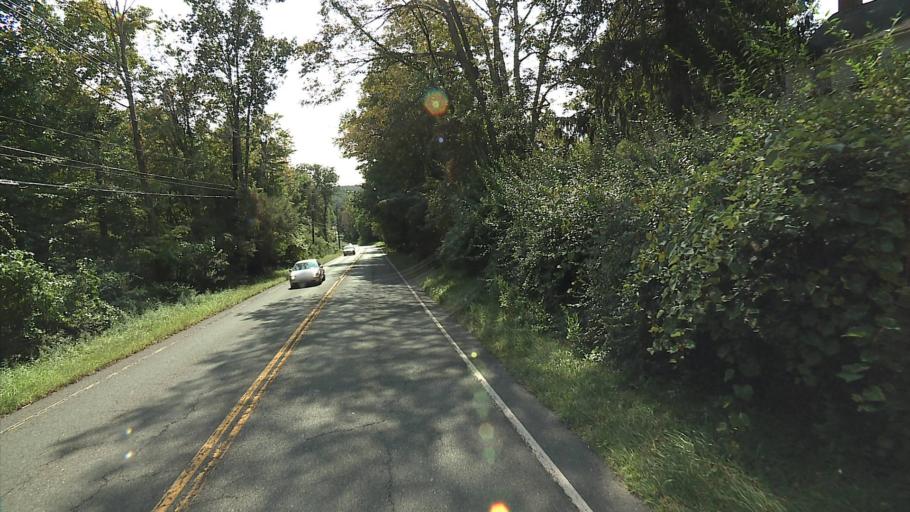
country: US
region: Connecticut
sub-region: New Haven County
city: Heritage Village
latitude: 41.4988
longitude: -73.2569
